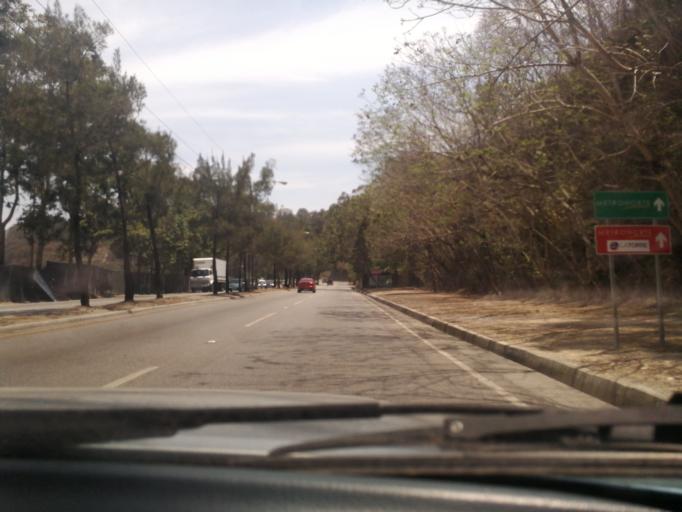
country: GT
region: Guatemala
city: Guatemala City
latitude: 14.6218
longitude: -90.4900
